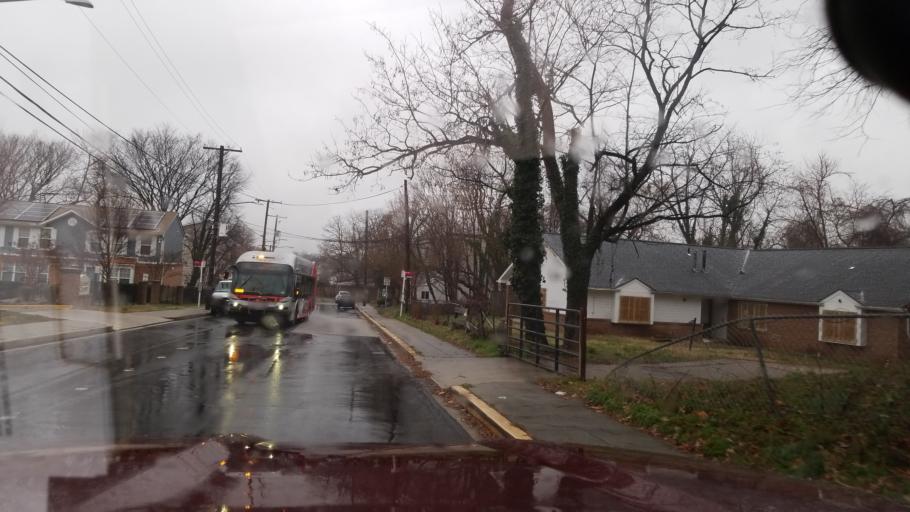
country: US
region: Maryland
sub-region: Prince George's County
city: Hillcrest Heights
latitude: 38.8541
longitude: -76.9876
